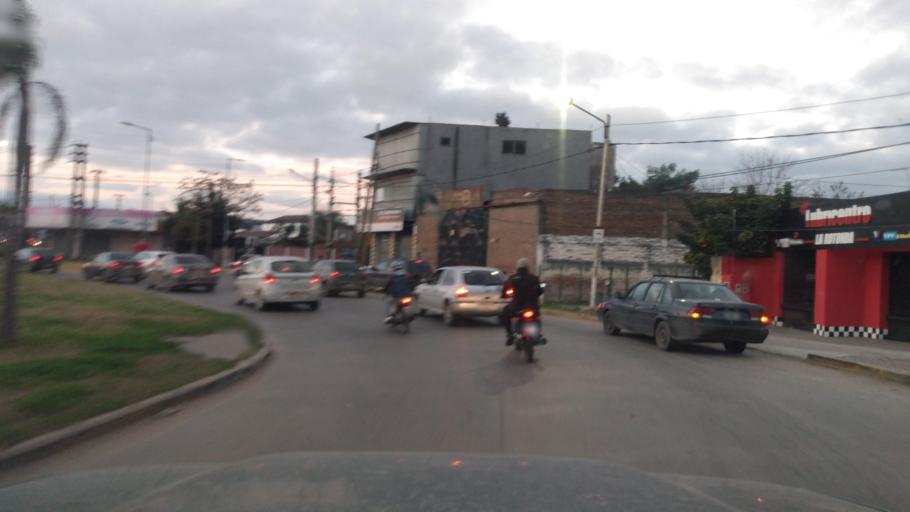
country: AR
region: Buenos Aires
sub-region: Partido de Pilar
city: Pilar
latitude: -34.4676
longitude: -58.9161
